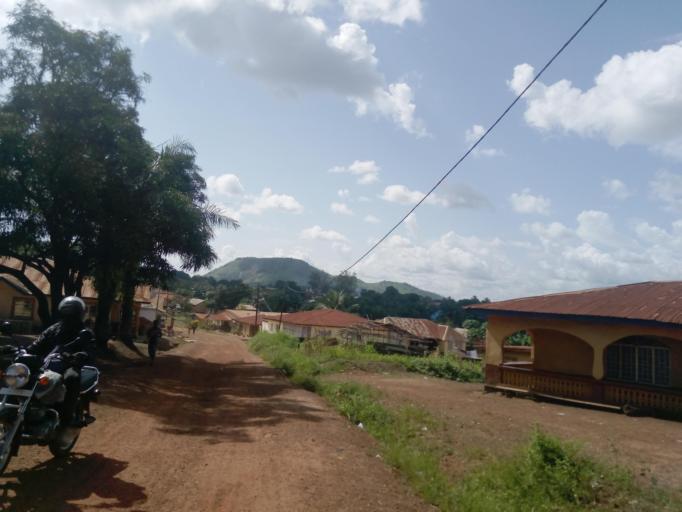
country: SL
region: Northern Province
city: Makeni
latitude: 8.8887
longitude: -12.0314
